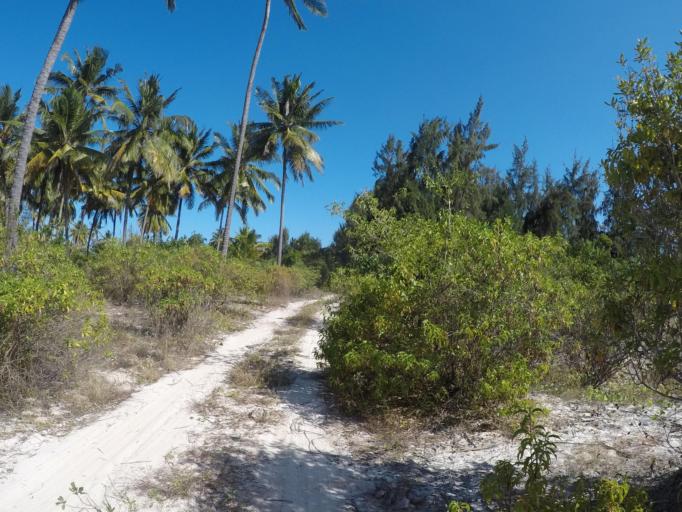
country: TZ
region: Zanzibar Central/South
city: Nganane
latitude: -6.2781
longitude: 39.5353
